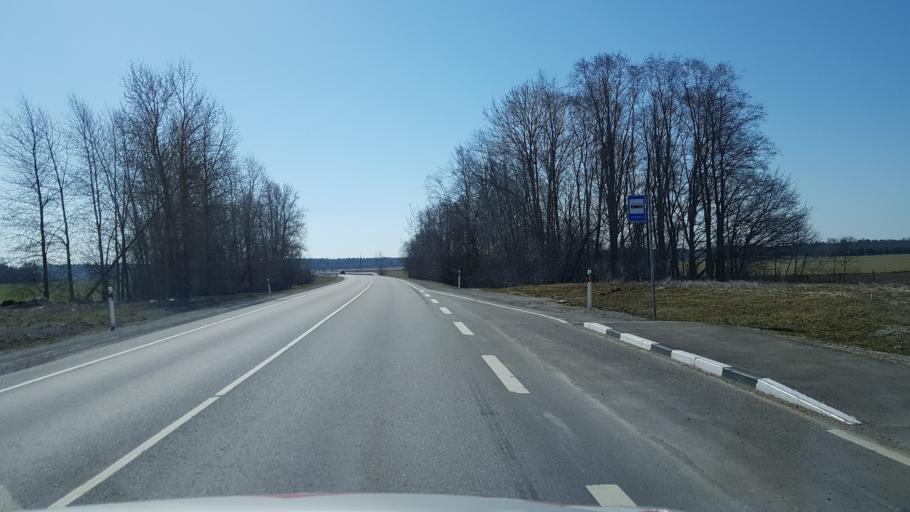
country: EE
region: Ida-Virumaa
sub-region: Kohtla-Jaerve linn
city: Kohtla-Jarve
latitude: 59.3500
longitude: 27.2419
